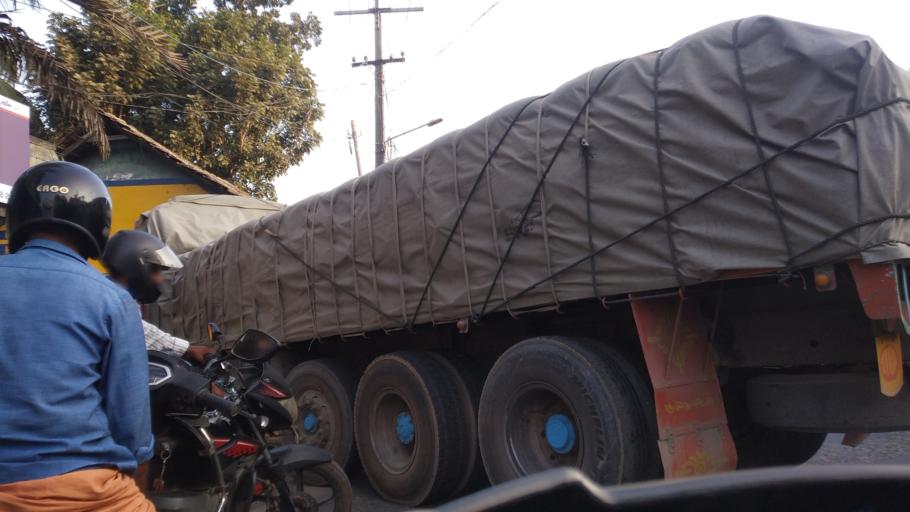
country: IN
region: Kerala
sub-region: Thrissur District
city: Kodungallur
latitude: 10.1498
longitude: 76.2239
